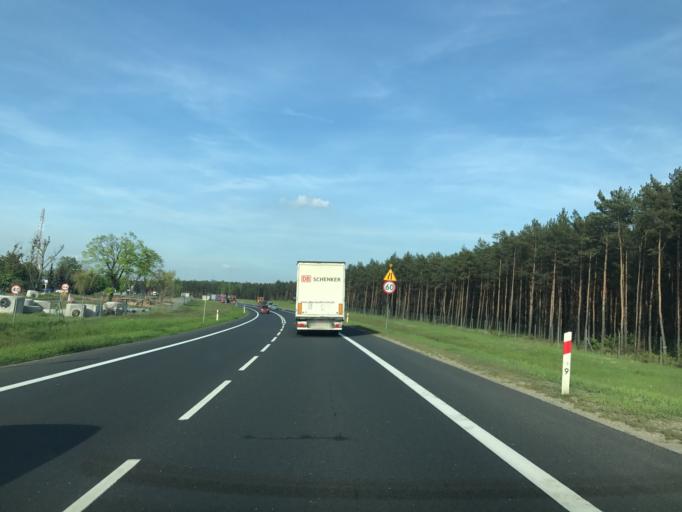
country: PL
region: Kujawsko-Pomorskie
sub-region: Powiat torunski
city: Wielka Nieszawka
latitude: 52.9678
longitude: 18.5602
